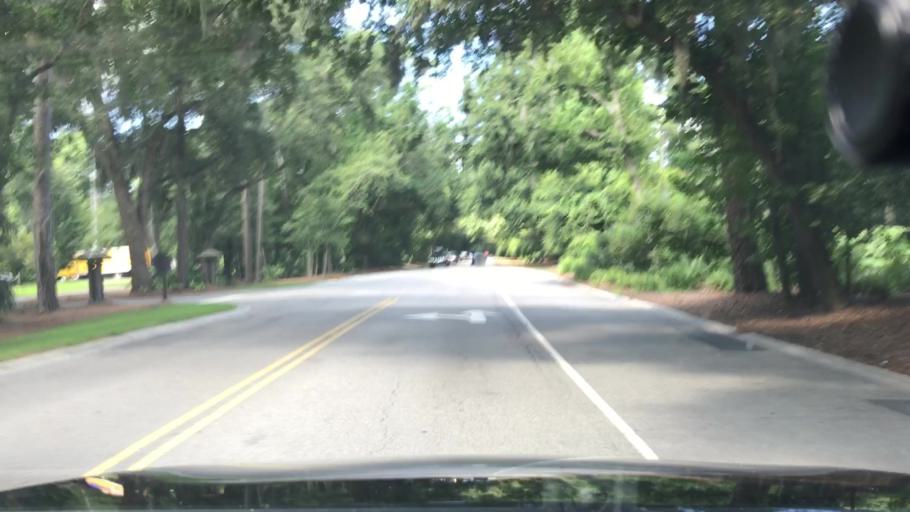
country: US
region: South Carolina
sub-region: Beaufort County
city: Hilton Head Island
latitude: 32.1513
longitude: -80.7744
